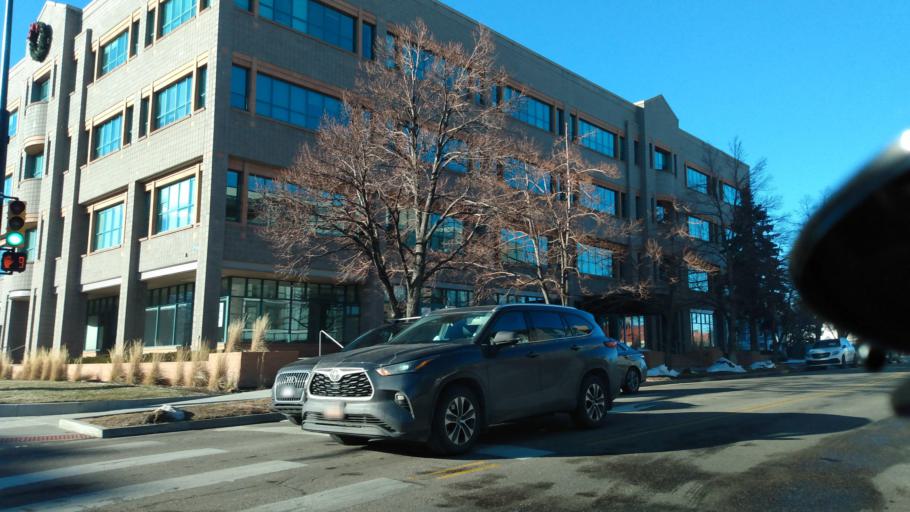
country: US
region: Colorado
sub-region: Boulder County
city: Boulder
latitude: 40.0176
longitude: -105.2605
